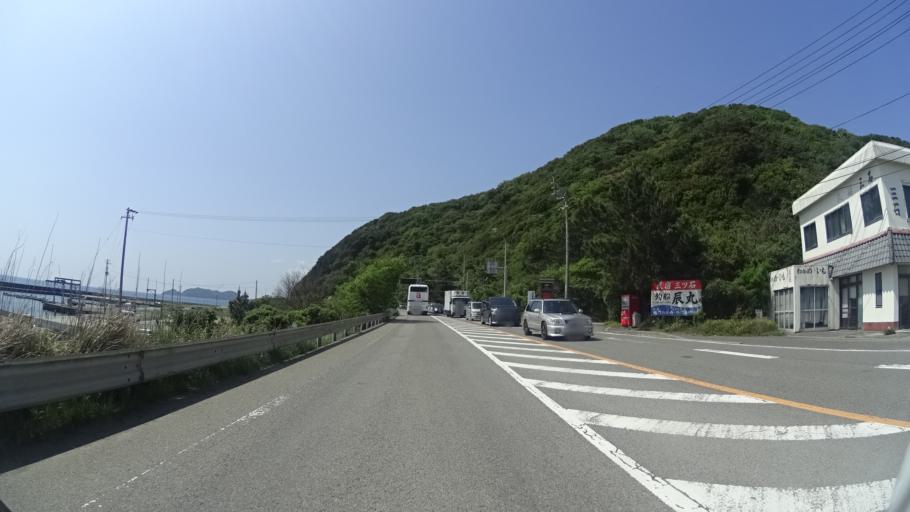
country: JP
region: Tokushima
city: Narutocho-mitsuishi
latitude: 34.2164
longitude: 134.6301
